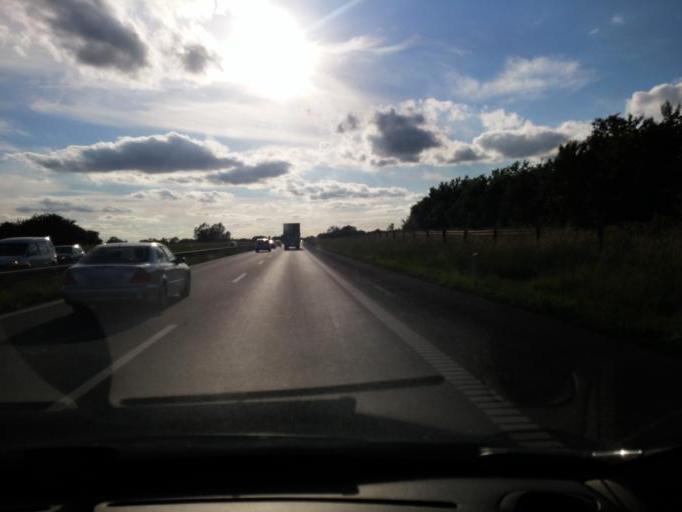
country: DK
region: South Denmark
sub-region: Nyborg Kommune
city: Ullerslev
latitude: 55.3347
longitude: 10.7155
